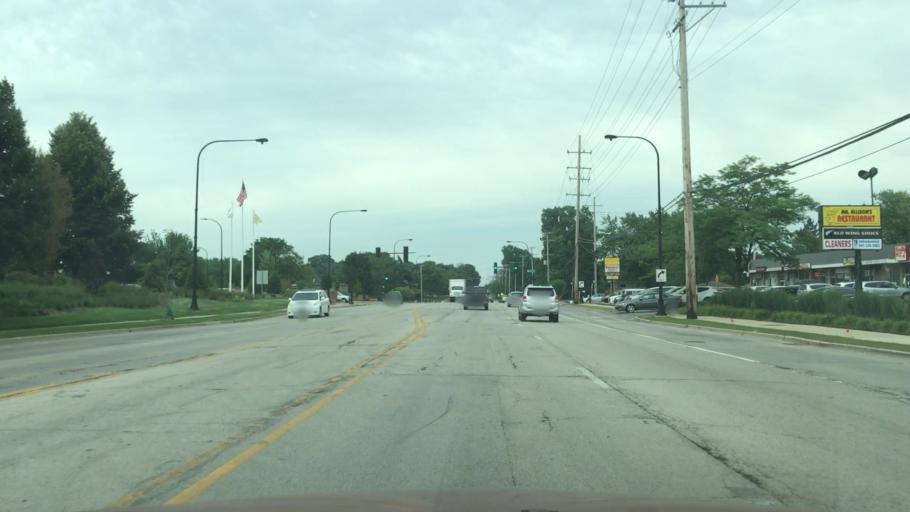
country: US
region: Illinois
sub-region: Cook County
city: Mount Prospect
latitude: 42.0664
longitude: -87.9619
